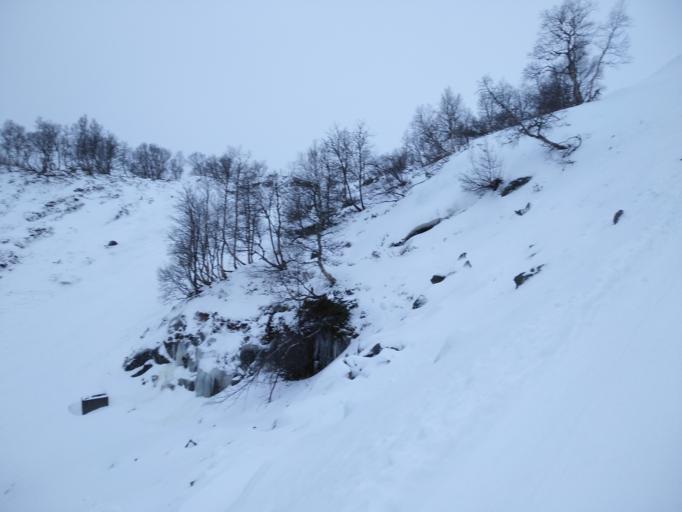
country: NO
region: Vest-Agder
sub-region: Sirdal
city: Tonstad
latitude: 59.0234
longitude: 6.9153
